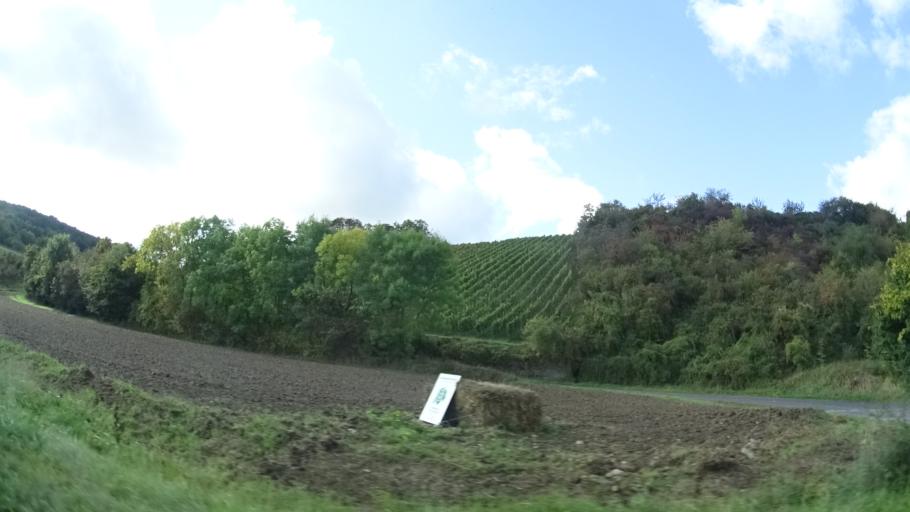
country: DE
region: Bavaria
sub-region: Regierungsbezirk Unterfranken
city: Mainstockheim
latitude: 49.7868
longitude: 10.1514
